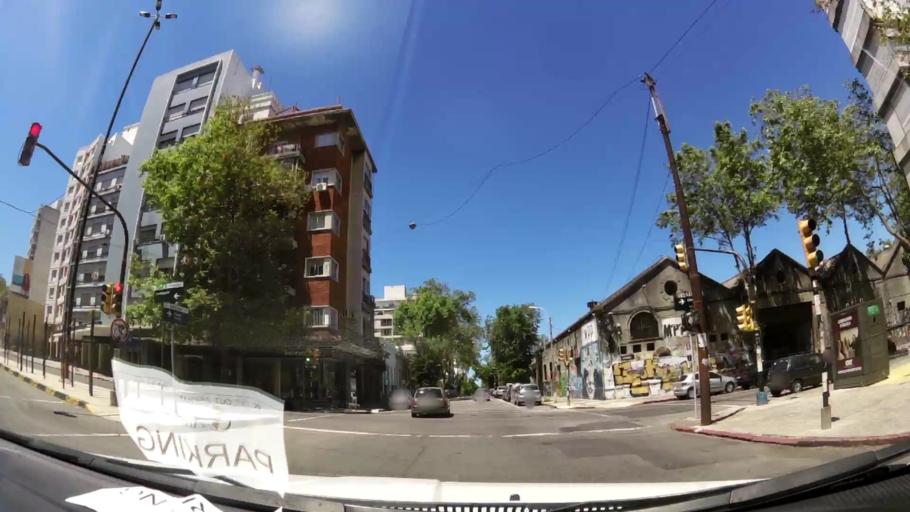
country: UY
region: Montevideo
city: Montevideo
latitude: -34.9074
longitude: -56.1743
